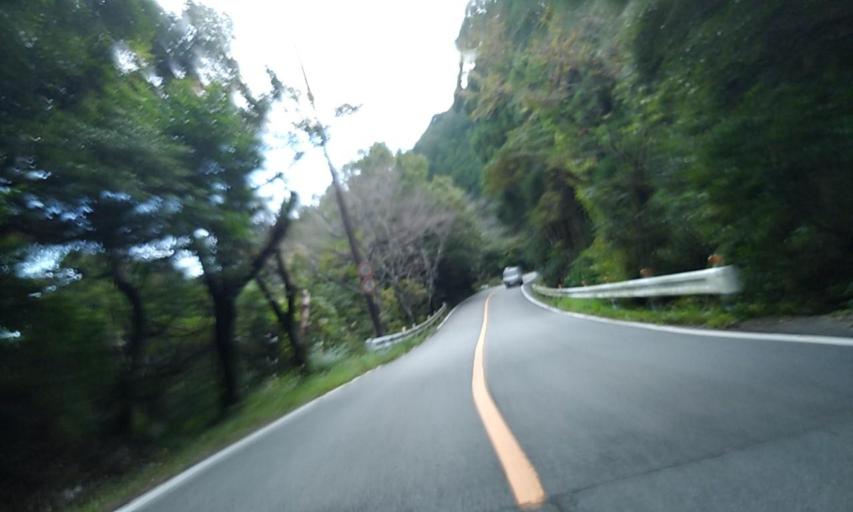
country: JP
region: Mie
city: Ise
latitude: 34.2883
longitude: 136.5359
